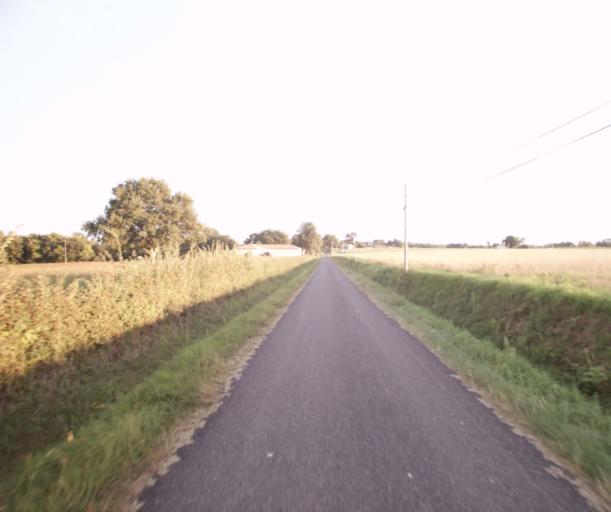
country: FR
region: Midi-Pyrenees
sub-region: Departement du Gers
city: Eauze
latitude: 43.8919
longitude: 0.0681
